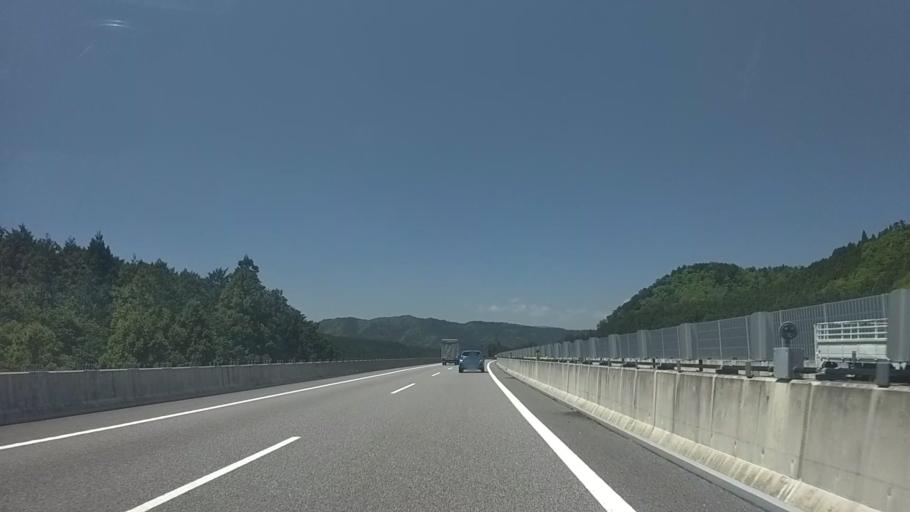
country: JP
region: Aichi
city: Shinshiro
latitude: 34.8929
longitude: 137.6336
